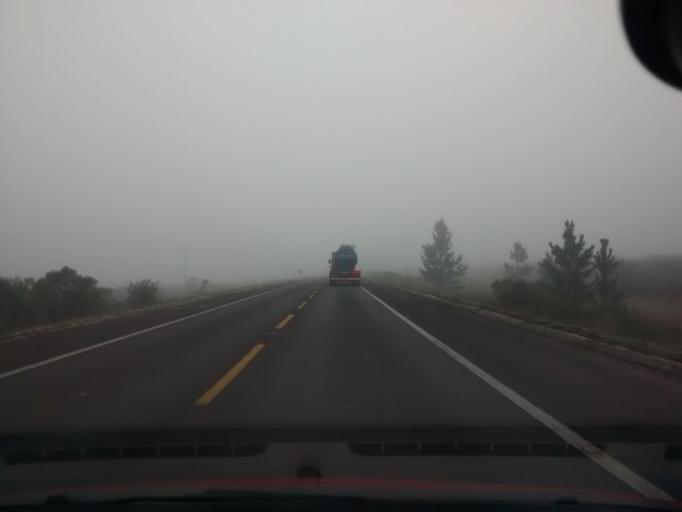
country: BR
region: Rio Grande do Sul
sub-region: Vacaria
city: Vacaria
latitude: -28.3770
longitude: -50.8394
